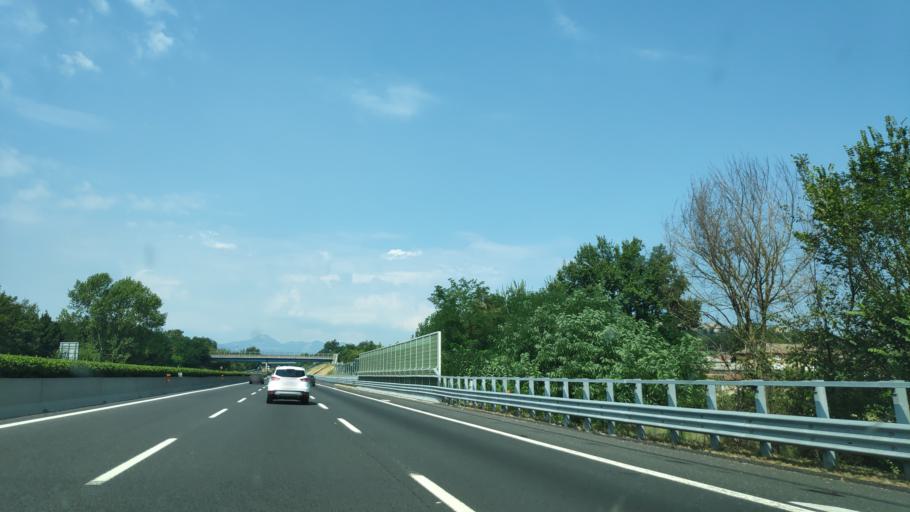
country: IT
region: Latium
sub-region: Provincia di Frosinone
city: Pofi
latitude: 41.5553
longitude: 13.4285
